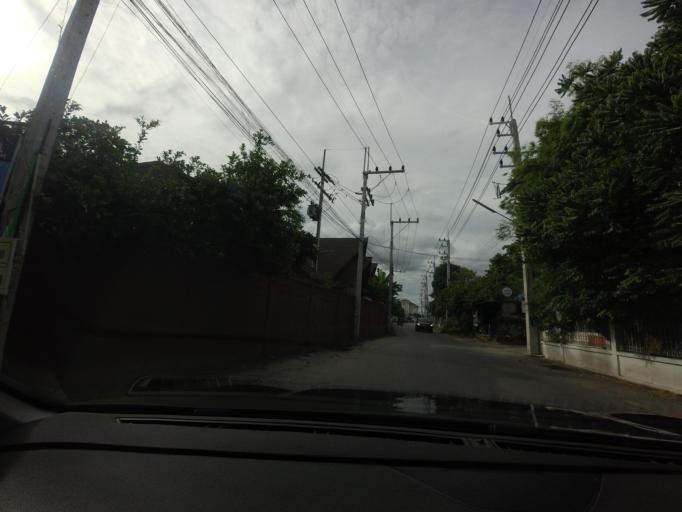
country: TH
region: Prachuap Khiri Khan
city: Hua Hin
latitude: 12.5565
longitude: 99.9551
